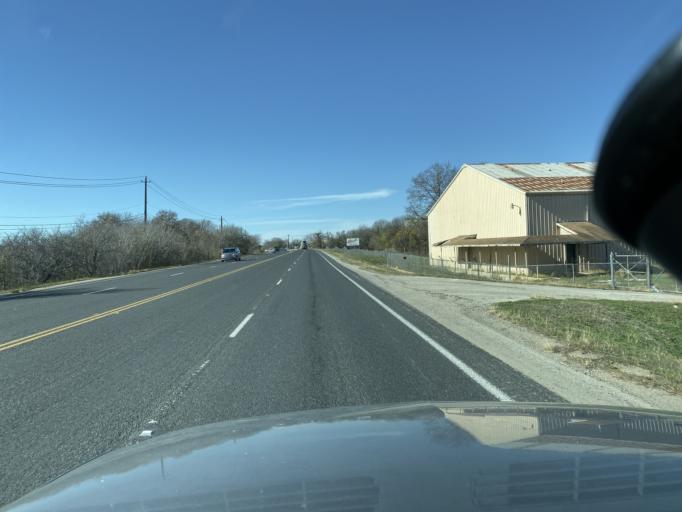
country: US
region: Texas
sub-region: Travis County
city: Garfield
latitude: 30.1718
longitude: -97.6669
